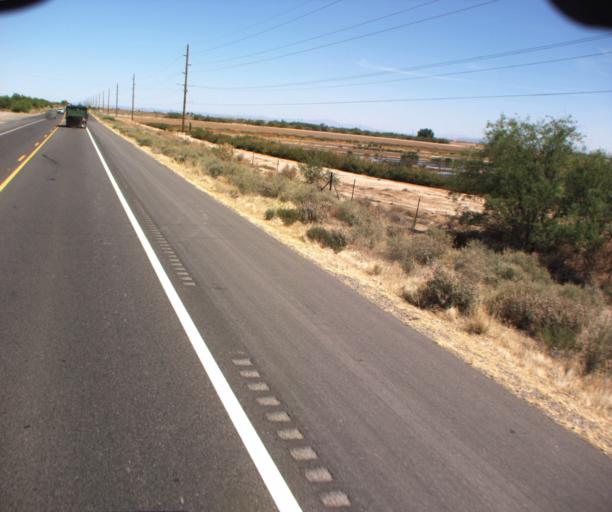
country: US
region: Arizona
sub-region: Pinal County
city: Blackwater
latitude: 33.0025
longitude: -111.5971
